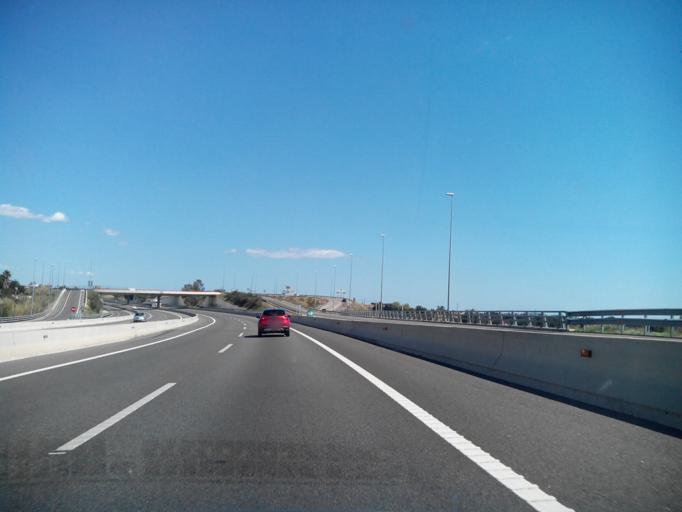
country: ES
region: Catalonia
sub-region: Provincia de Tarragona
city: Cambrils
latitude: 41.0830
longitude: 1.0734
